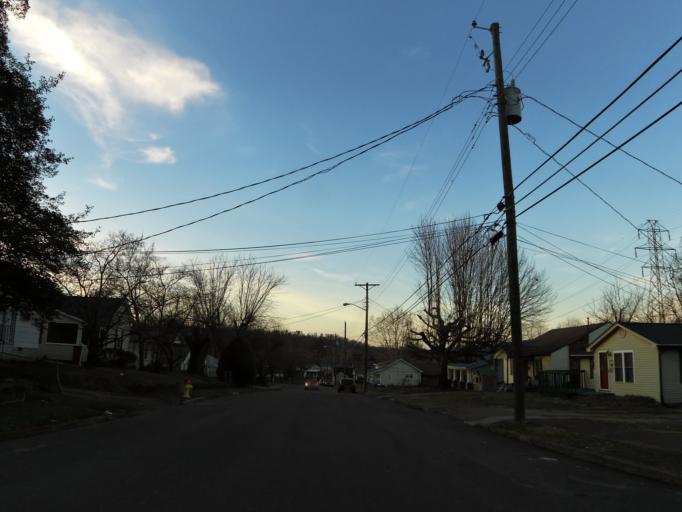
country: US
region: Tennessee
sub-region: Knox County
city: Knoxville
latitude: 36.0004
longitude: -83.9178
